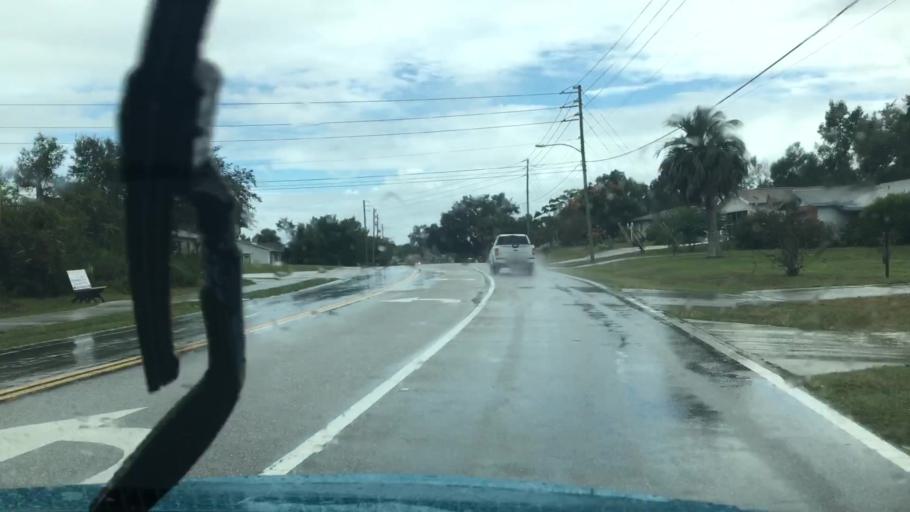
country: US
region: Florida
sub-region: Volusia County
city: Deltona
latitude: 28.8936
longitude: -81.2497
